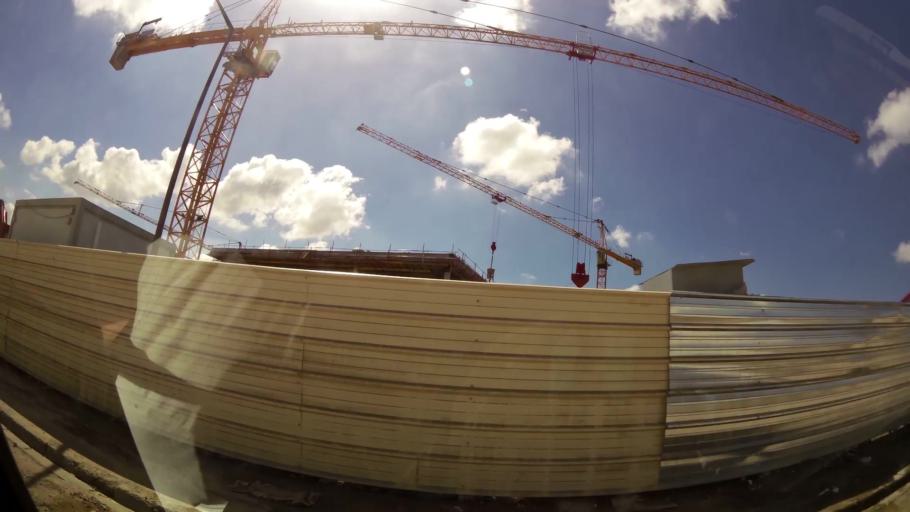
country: MA
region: Grand Casablanca
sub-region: Nouaceur
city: Bouskoura
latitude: 33.4895
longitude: -7.6054
